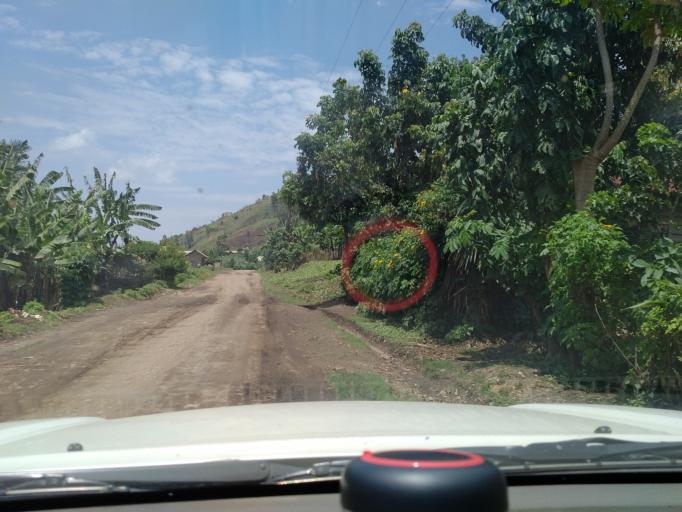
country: CD
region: Nord Kivu
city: Sake
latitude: -1.6385
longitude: 29.0285
